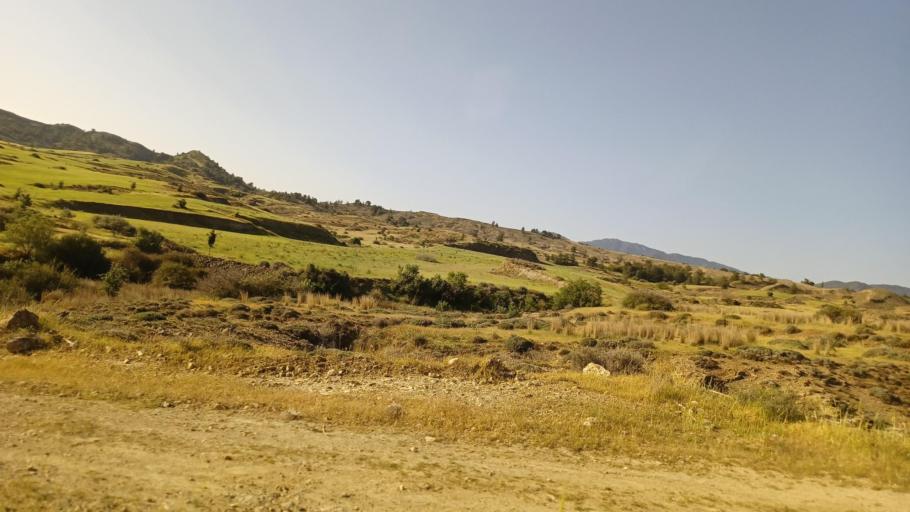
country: CY
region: Lefkosia
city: Astromeritis
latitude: 35.0802
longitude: 33.0275
